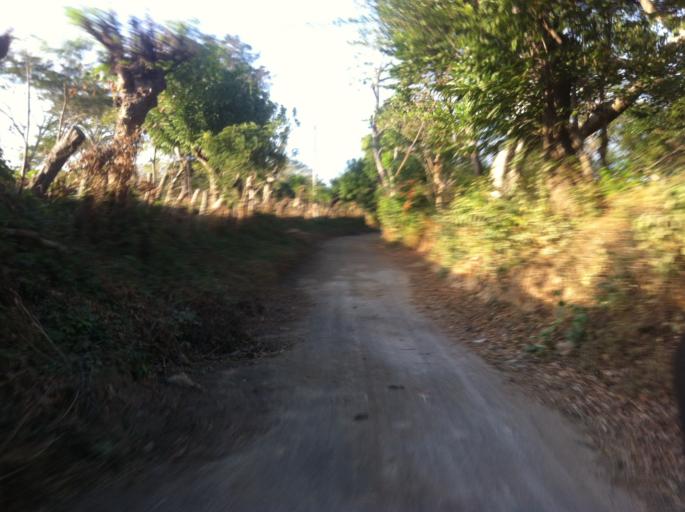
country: NI
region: Managua
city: Managua
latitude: 12.0772
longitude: -86.3097
